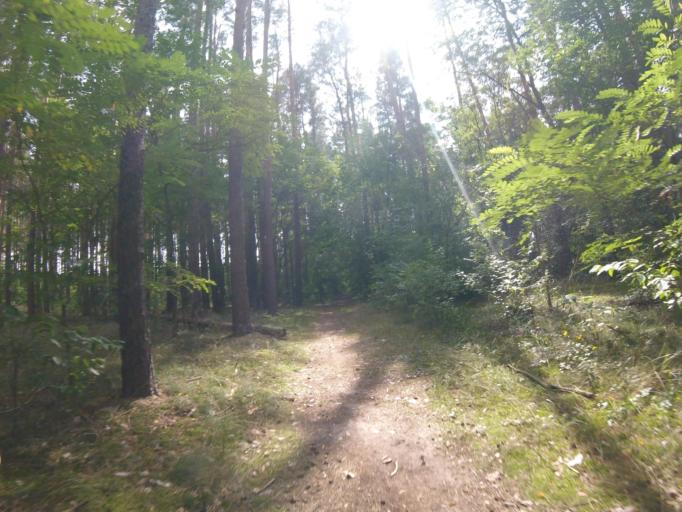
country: DE
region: Brandenburg
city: Bestensee
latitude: 52.2652
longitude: 13.6630
